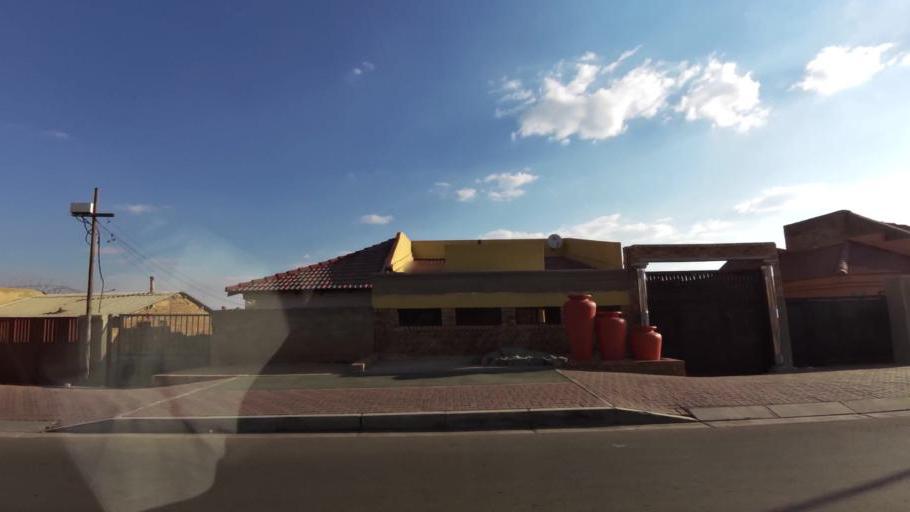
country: ZA
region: Gauteng
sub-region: City of Johannesburg Metropolitan Municipality
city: Soweto
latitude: -26.2280
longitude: 27.8943
